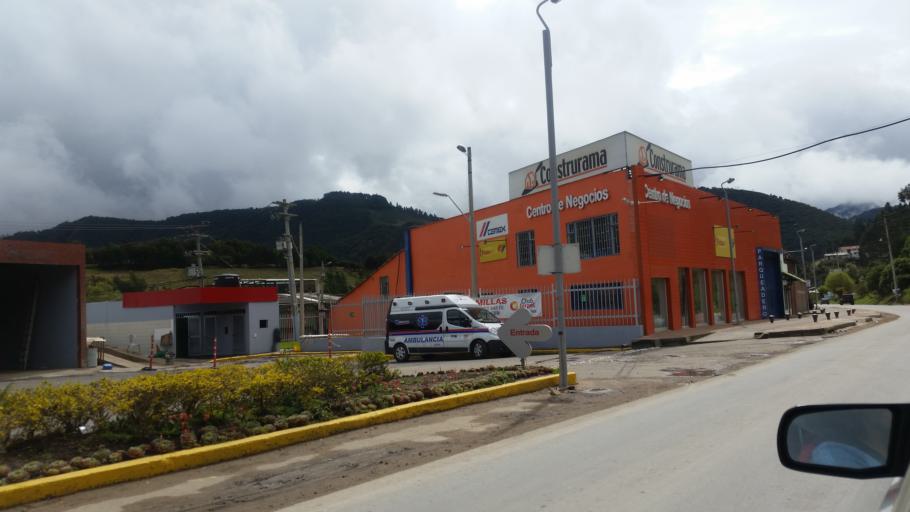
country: CO
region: Cundinamarca
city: La Calera
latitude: 4.7240
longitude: -73.9592
